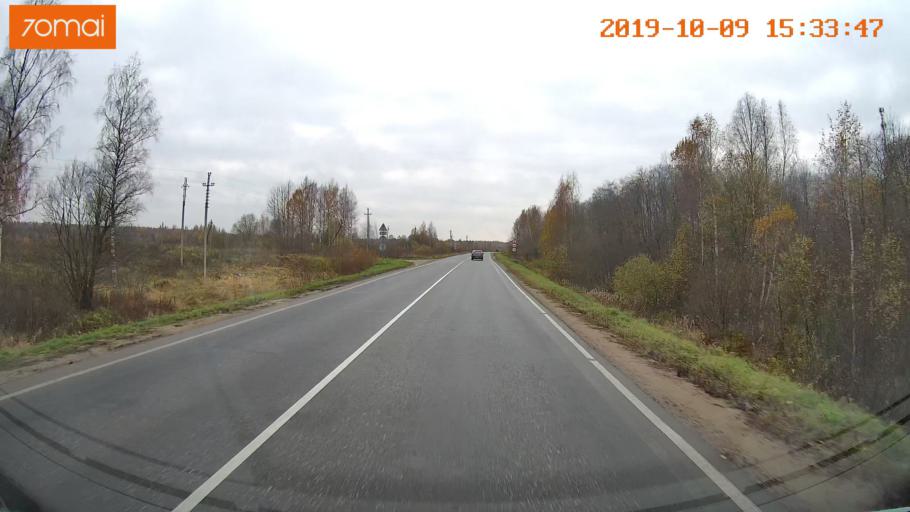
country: RU
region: Kostroma
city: Oktyabr'skiy
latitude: 57.9473
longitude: 41.2574
